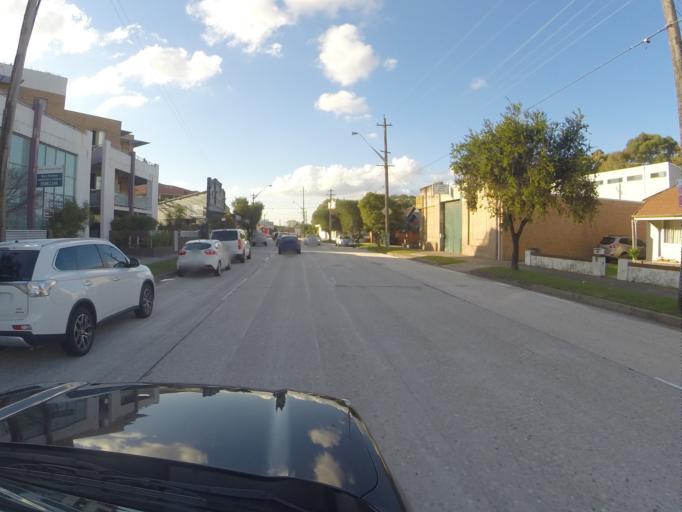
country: AU
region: New South Wales
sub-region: Rockdale
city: Bexley
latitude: -33.9571
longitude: 151.1181
